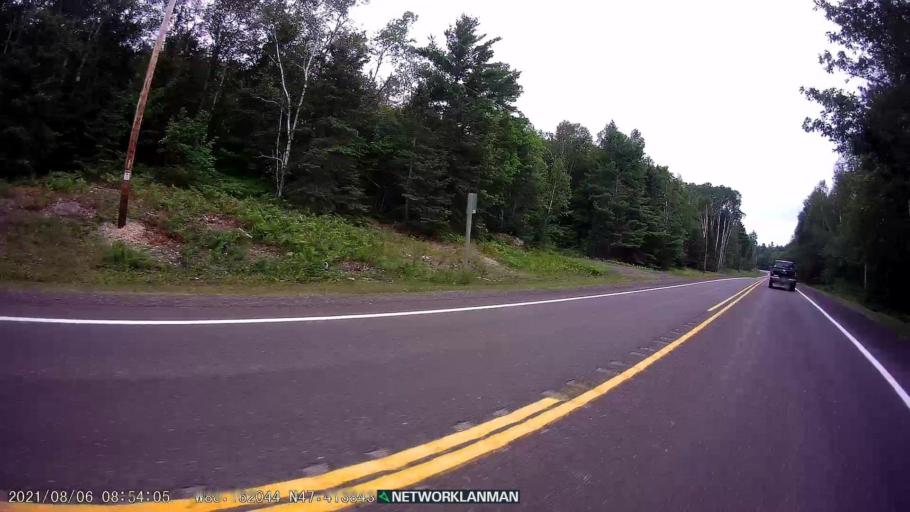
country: US
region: Michigan
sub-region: Keweenaw County
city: Eagle River
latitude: 47.4142
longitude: -88.1612
